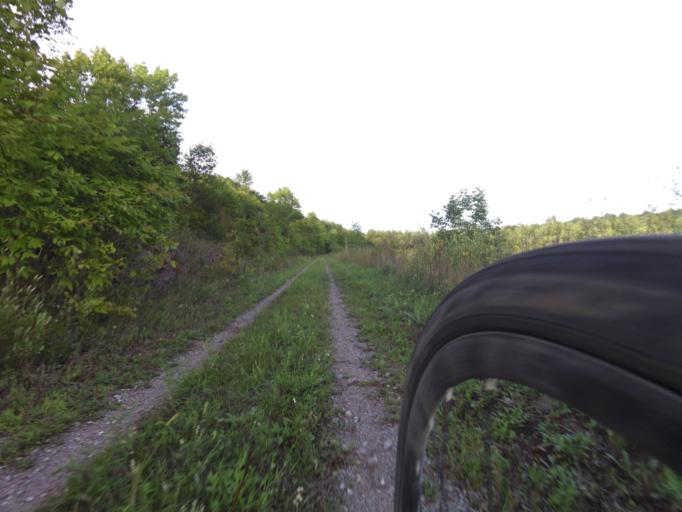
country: CA
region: Ontario
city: Gananoque
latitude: 44.5560
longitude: -76.3788
